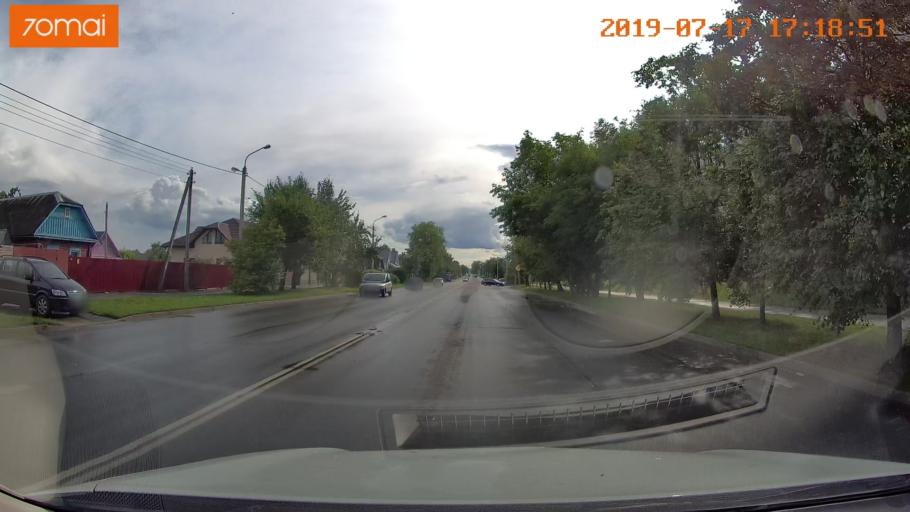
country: BY
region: Mogilev
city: Babruysk
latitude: 53.1596
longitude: 29.1976
